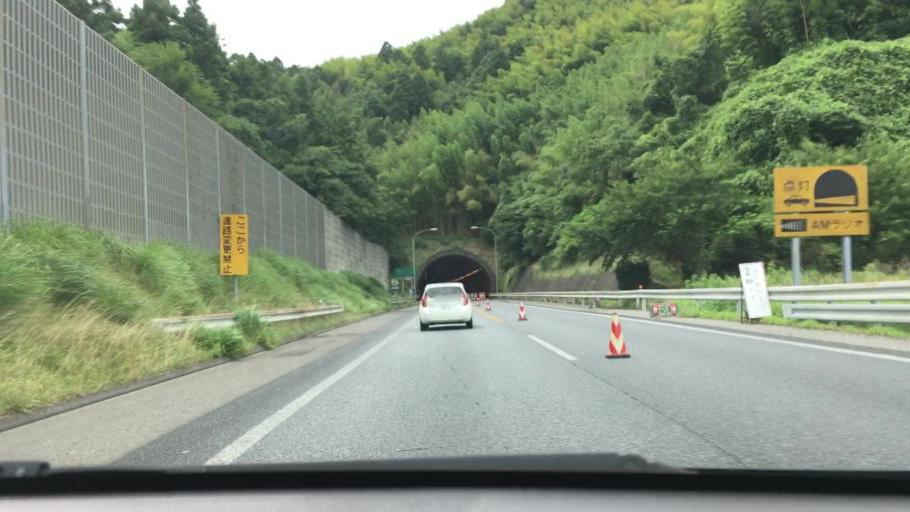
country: JP
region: Yamaguchi
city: Tokuyama
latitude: 34.0885
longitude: 131.7769
